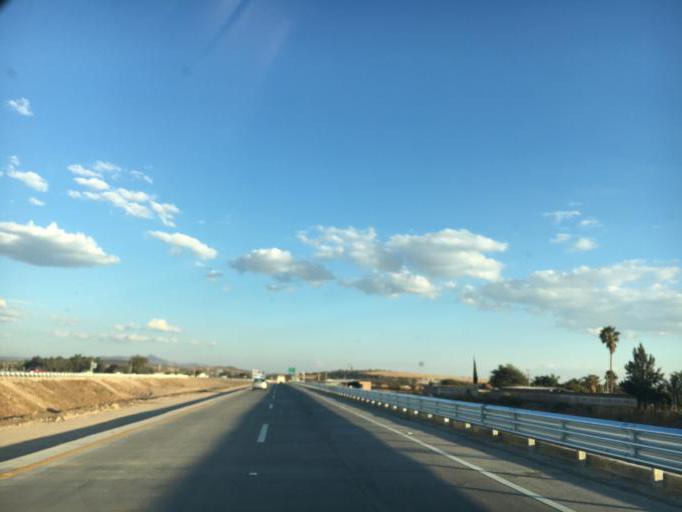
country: MX
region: Guanajuato
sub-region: Leon
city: Ladrilleras del Refugio
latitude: 21.0795
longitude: -101.5488
